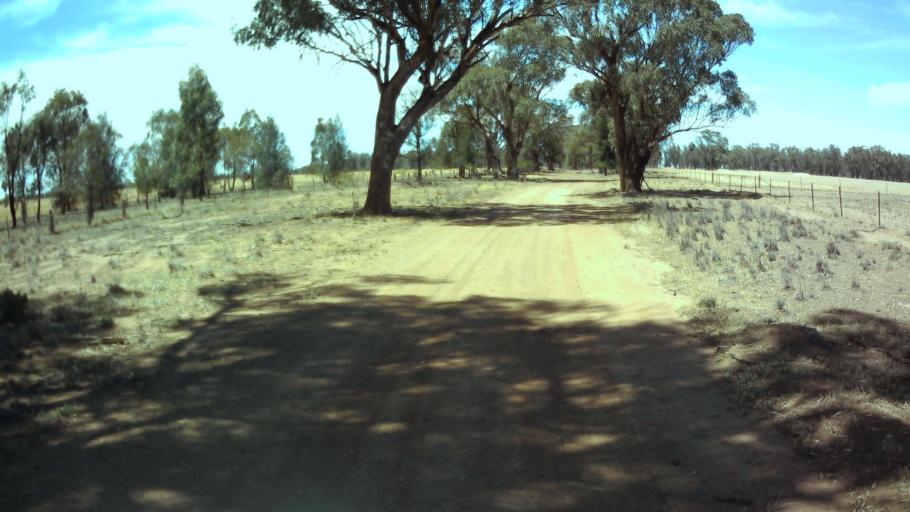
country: AU
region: New South Wales
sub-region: Weddin
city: Grenfell
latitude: -33.9042
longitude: 147.8077
